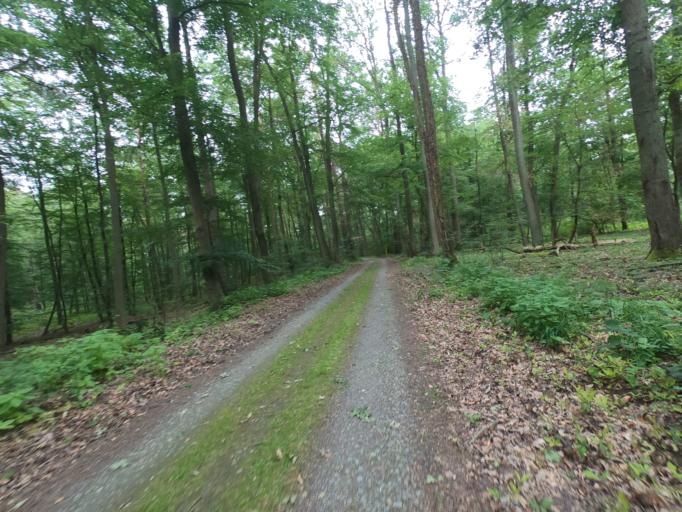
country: DE
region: Hesse
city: Niederrad
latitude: 50.0356
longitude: 8.6420
